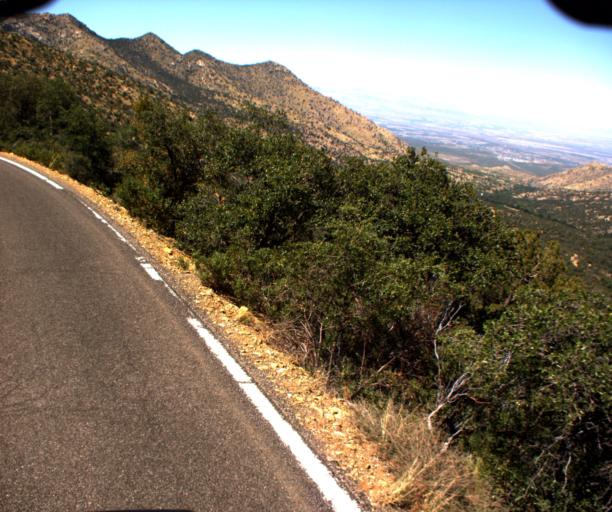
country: US
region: Arizona
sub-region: Graham County
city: Swift Trail Junction
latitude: 32.6540
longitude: -109.8048
